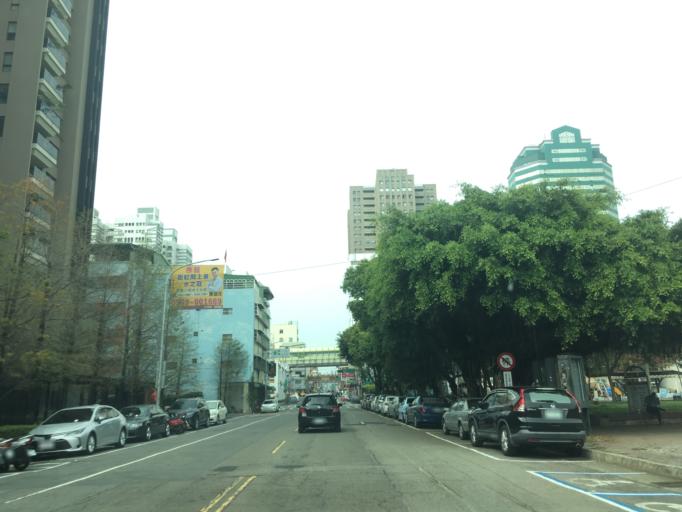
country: TW
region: Taiwan
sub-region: Taichung City
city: Taichung
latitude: 24.1693
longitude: 120.6941
